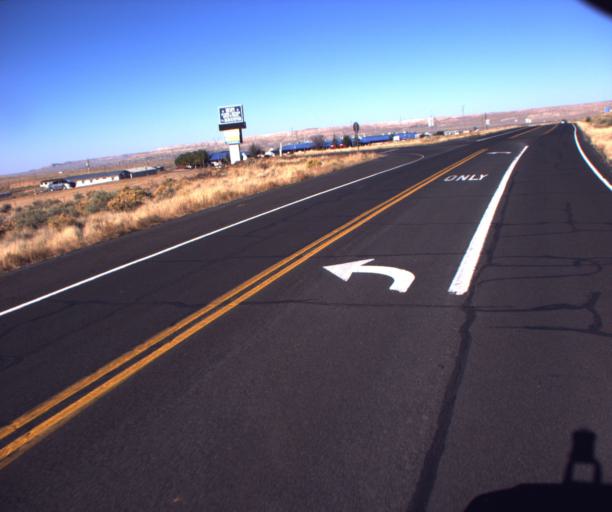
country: US
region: Arizona
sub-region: Navajo County
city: First Mesa
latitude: 35.8317
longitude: -110.2932
